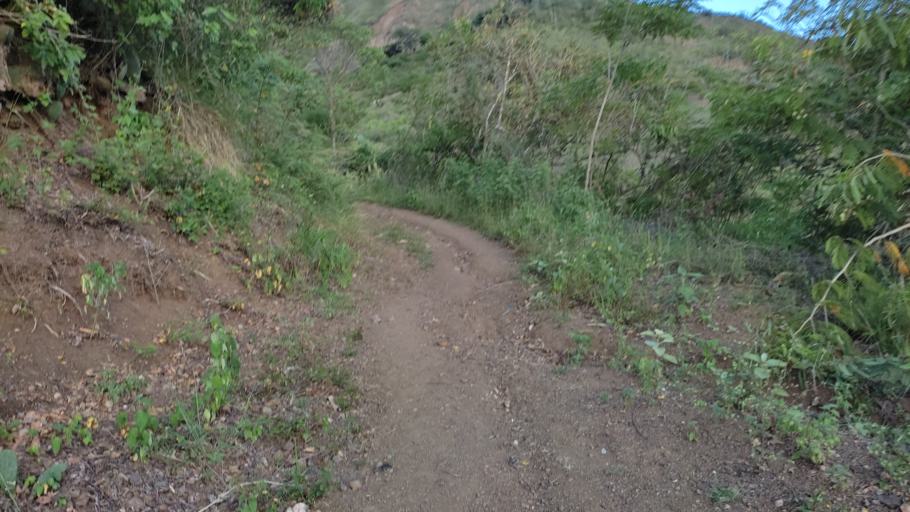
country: CO
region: Narino
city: Taminango
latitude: 1.5435
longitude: -77.3691
